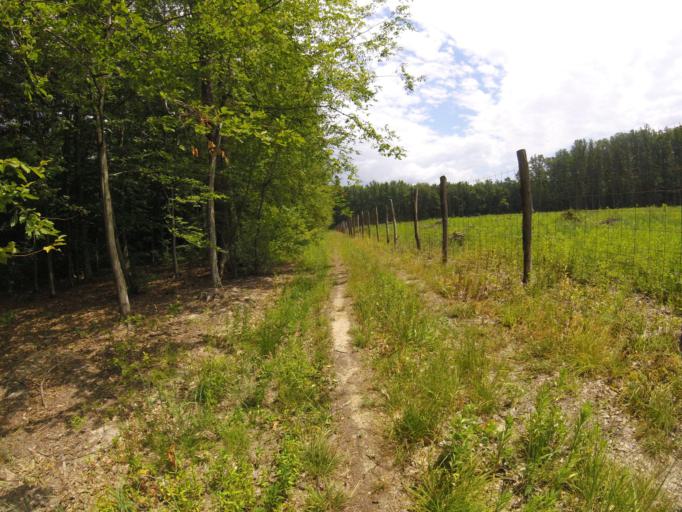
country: HU
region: Zala
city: Turje
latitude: 47.0342
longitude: 17.0515
